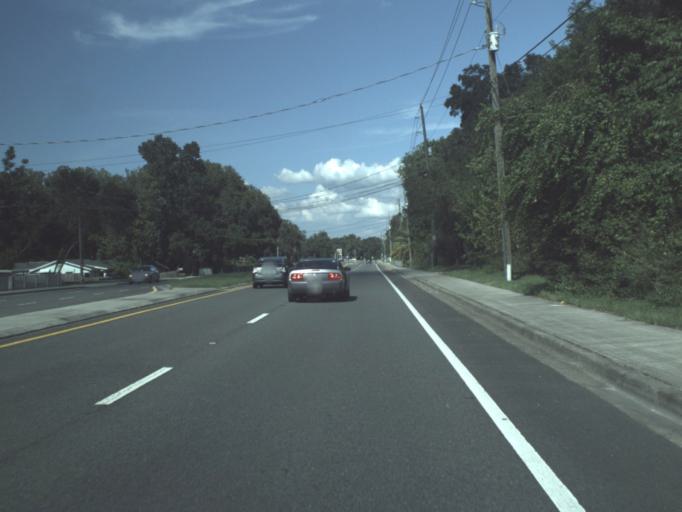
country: US
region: Florida
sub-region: Citrus County
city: Inverness
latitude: 28.8457
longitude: -82.2807
